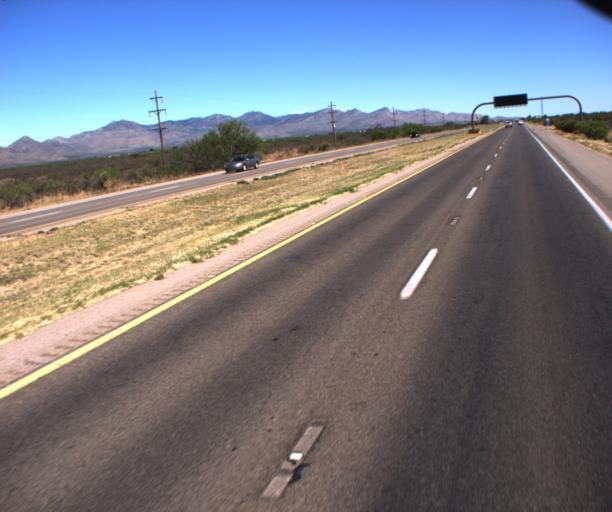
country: US
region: Arizona
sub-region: Cochise County
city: Huachuca City
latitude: 31.6689
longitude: -110.3502
